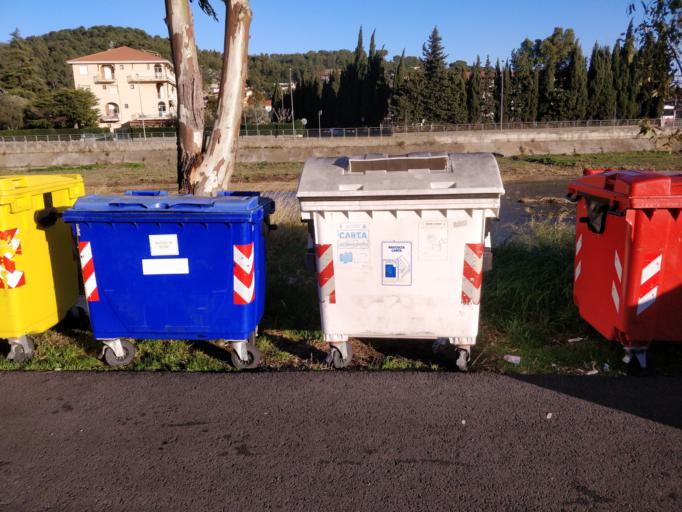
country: IT
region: Liguria
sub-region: Provincia di Savona
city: Andora
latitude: 43.9580
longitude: 8.1410
